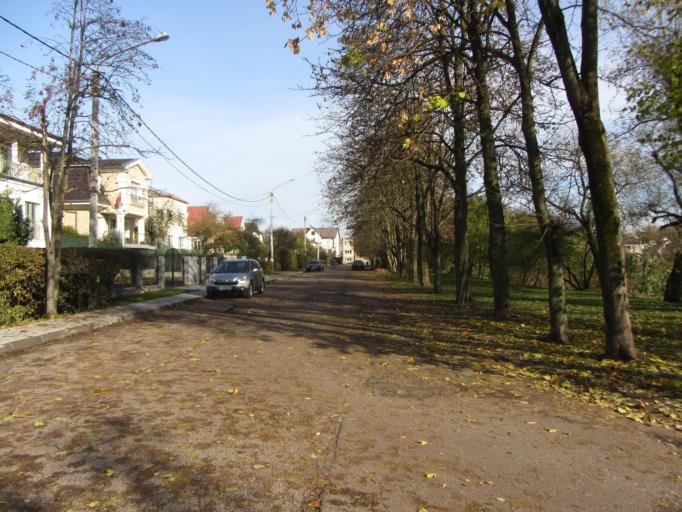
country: LT
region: Vilnius County
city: Seskine
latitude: 54.6952
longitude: 25.2435
